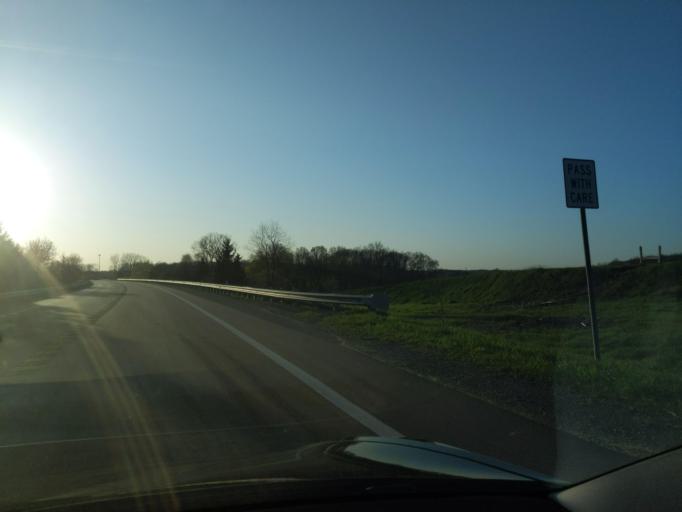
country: US
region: Michigan
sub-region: Washtenaw County
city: Chelsea
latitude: 42.3887
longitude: -84.0912
